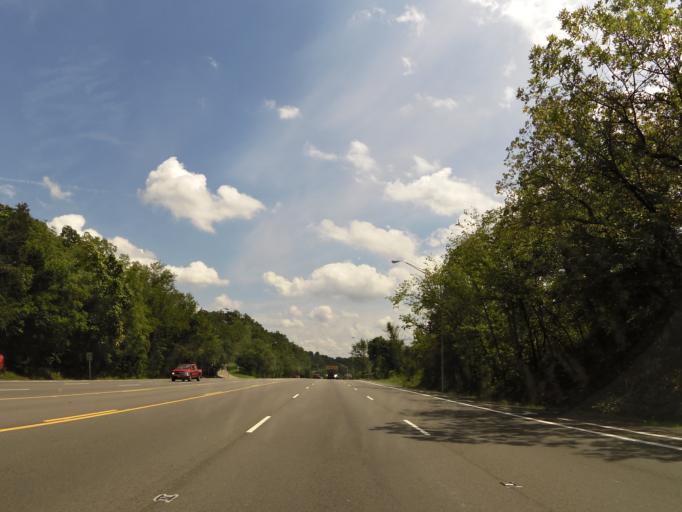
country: US
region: Tennessee
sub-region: Sullivan County
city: Kingsport
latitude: 36.5589
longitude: -82.5480
